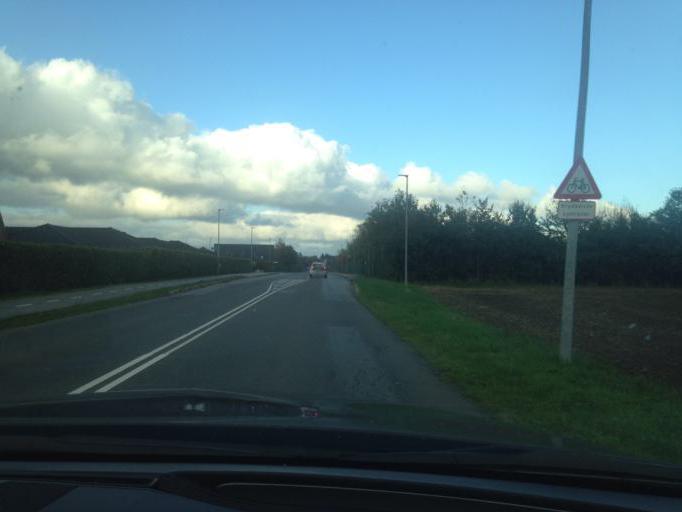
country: DK
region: South Denmark
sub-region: Kolding Kommune
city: Kolding
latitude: 55.5590
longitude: 9.4866
